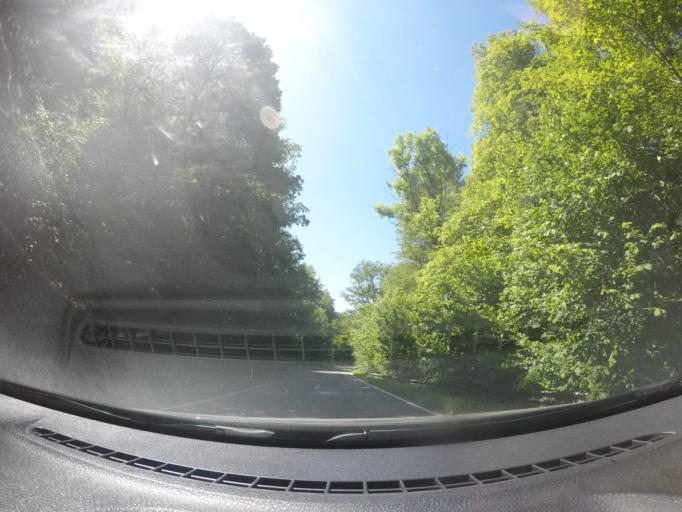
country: BE
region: Wallonia
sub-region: Province du Luxembourg
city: Daverdisse
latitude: 50.0451
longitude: 5.1452
